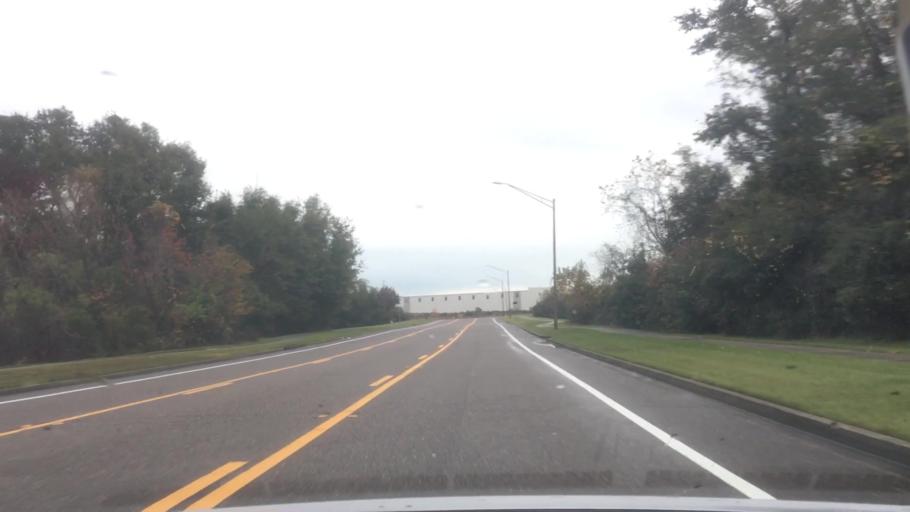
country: US
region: Florida
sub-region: Duval County
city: Jacksonville
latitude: 30.4493
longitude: -81.5745
